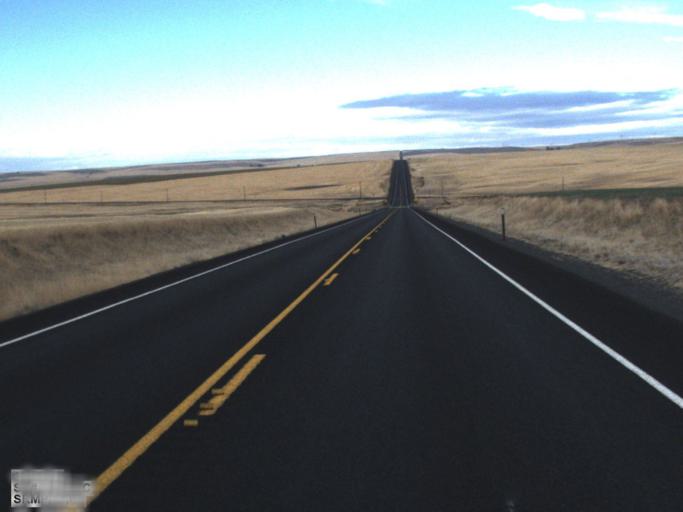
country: US
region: Washington
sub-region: Okanogan County
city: Coulee Dam
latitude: 47.8051
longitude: -118.7619
